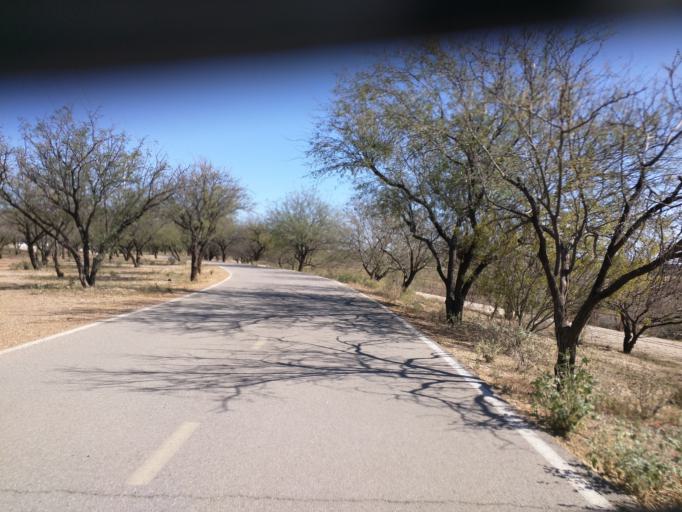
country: US
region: Arizona
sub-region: Pima County
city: Flowing Wells
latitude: 32.2992
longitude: -111.0049
